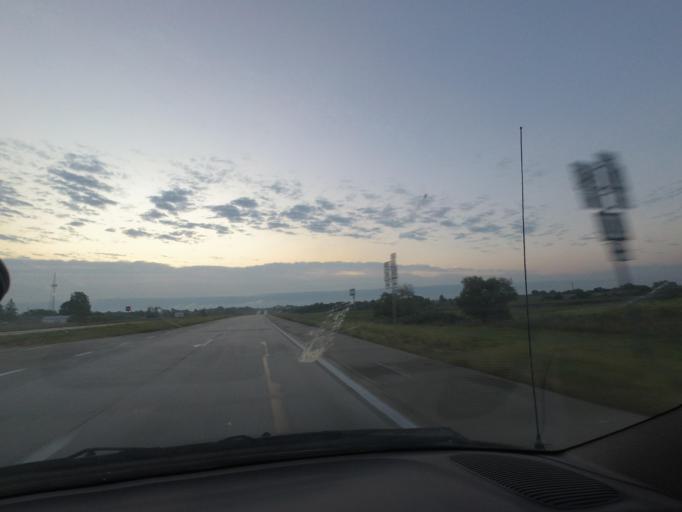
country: US
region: Missouri
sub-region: Macon County
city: Macon
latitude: 39.7580
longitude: -92.6411
